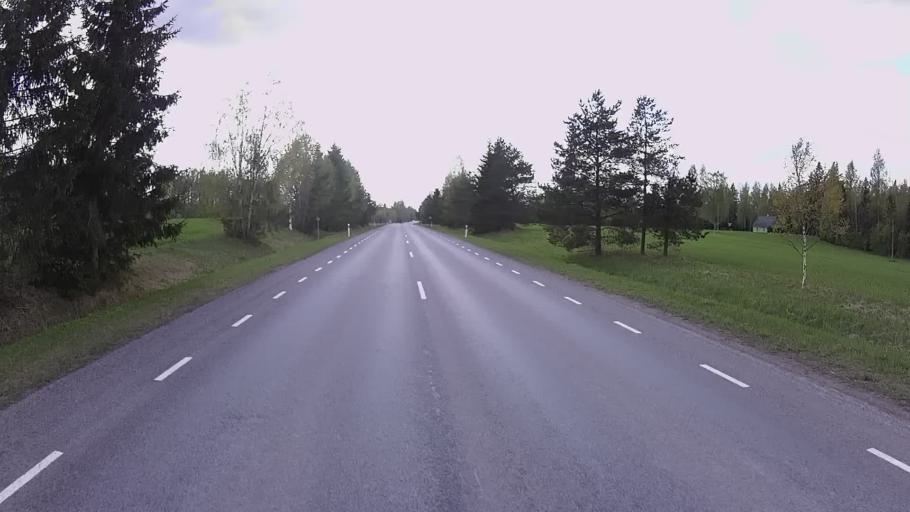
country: EE
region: Tartu
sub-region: Alatskivi vald
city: Kallaste
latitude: 58.5147
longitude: 26.9800
